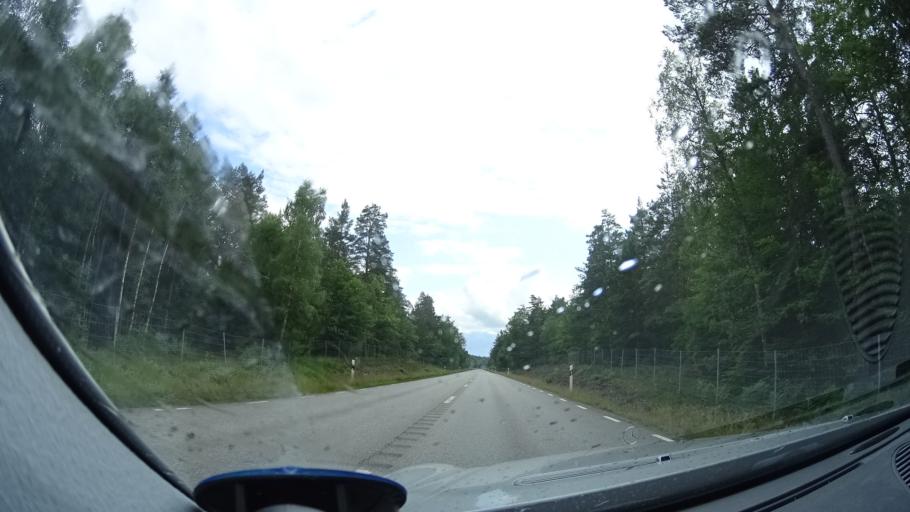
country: SE
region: Blekinge
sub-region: Karlshamns Kommun
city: Svangsta
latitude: 56.2446
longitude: 14.8280
